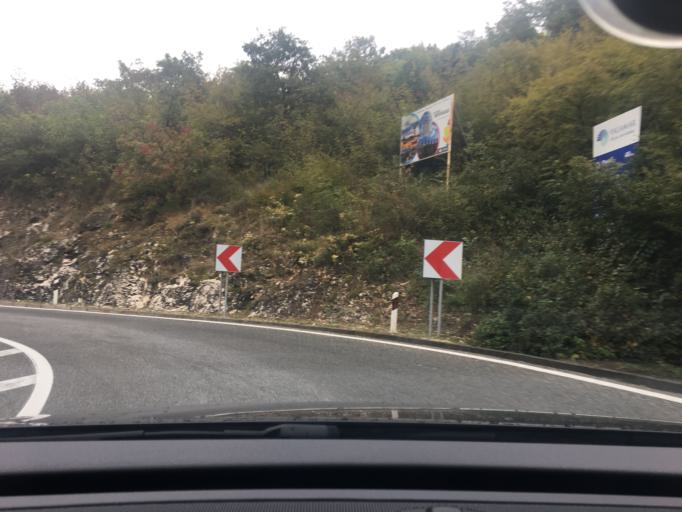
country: HR
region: Istarska
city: Buje
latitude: 45.4518
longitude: 13.6493
